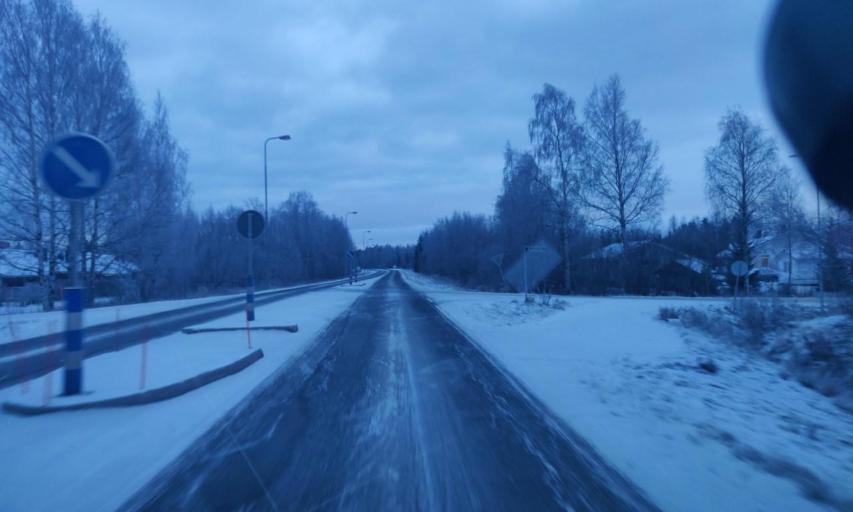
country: FI
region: Northern Ostrobothnia
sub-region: Oulu
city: Oulunsalo
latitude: 64.9744
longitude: 25.3222
